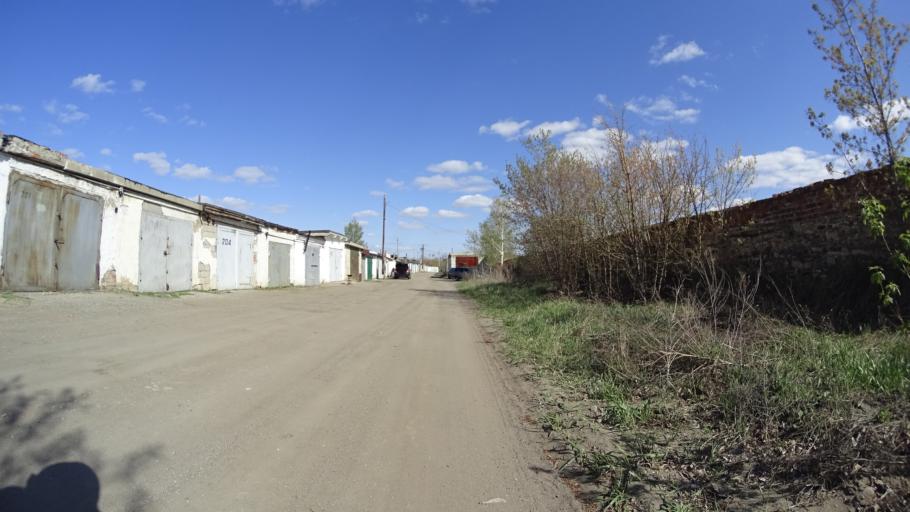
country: RU
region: Chelyabinsk
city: Troitsk
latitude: 54.0829
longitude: 61.5273
